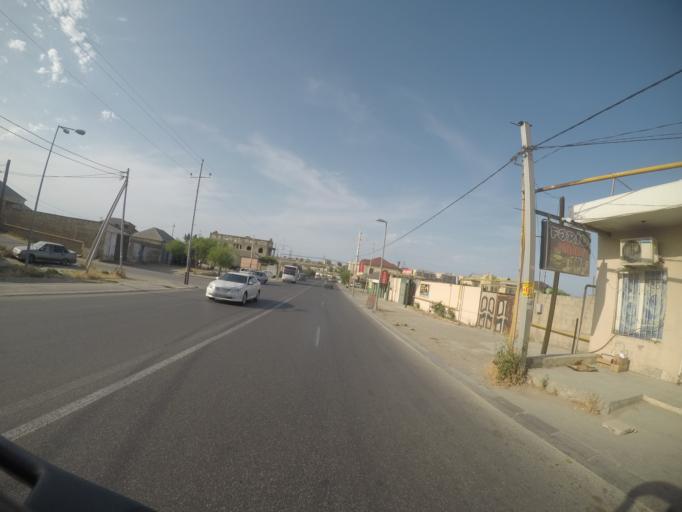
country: AZ
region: Baki
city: Binagadi
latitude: 40.4775
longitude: 49.8335
